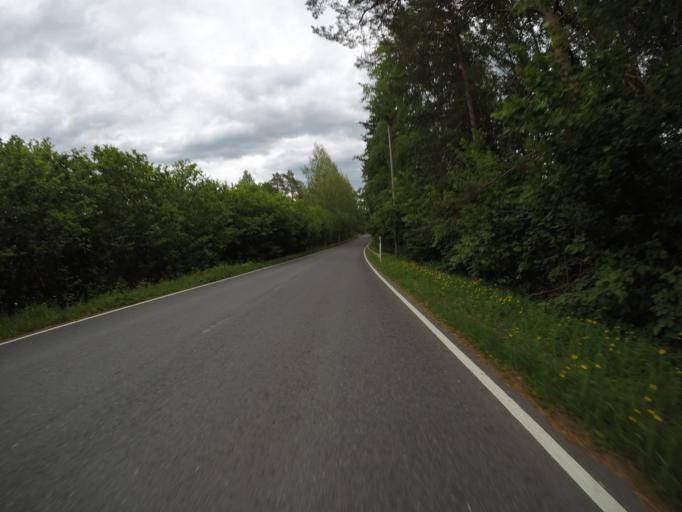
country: FI
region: Haeme
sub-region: Haemeenlinna
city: Haemeenlinna
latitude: 60.9761
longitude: 24.4598
